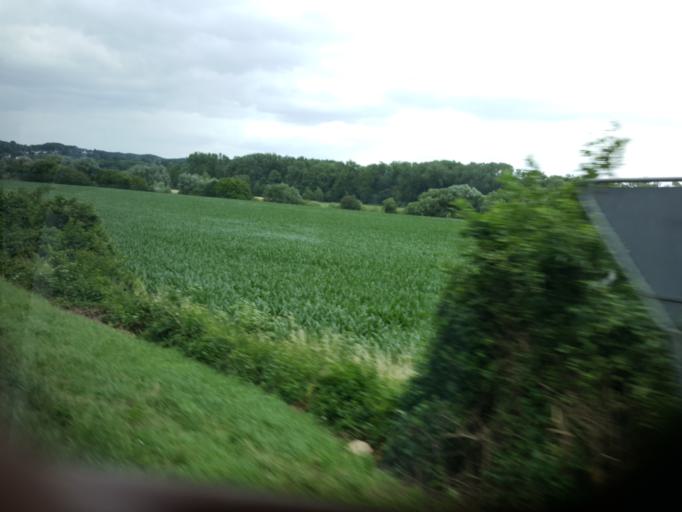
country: DE
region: North Rhine-Westphalia
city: Porta Westfalica
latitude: 52.2417
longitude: 8.8948
